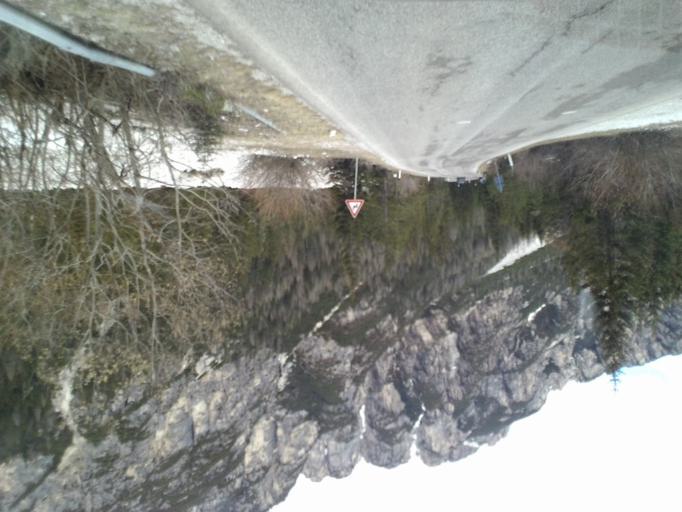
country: IT
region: Veneto
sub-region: Provincia di Belluno
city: Cortina d'Ampezzo
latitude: 46.5996
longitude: 12.2424
